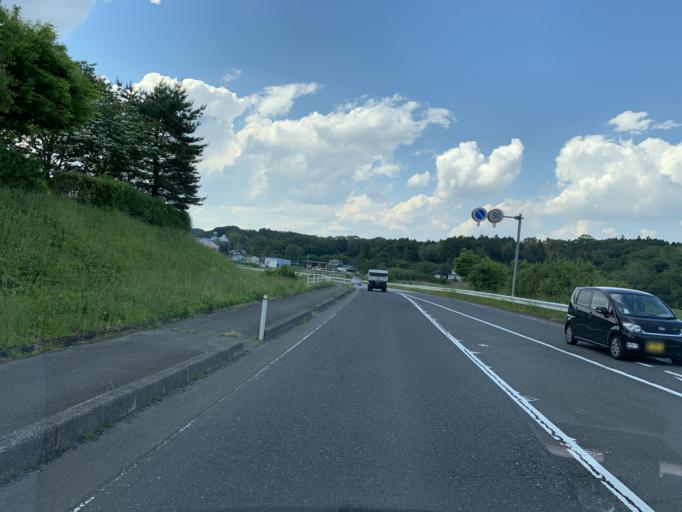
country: JP
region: Miyagi
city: Wakuya
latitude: 38.5407
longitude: 141.1497
